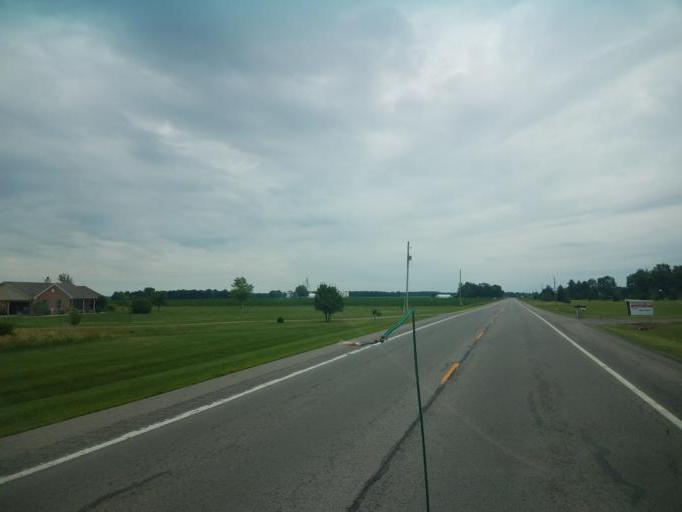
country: US
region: Ohio
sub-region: Hardin County
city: Ada
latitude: 40.7309
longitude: -83.7940
